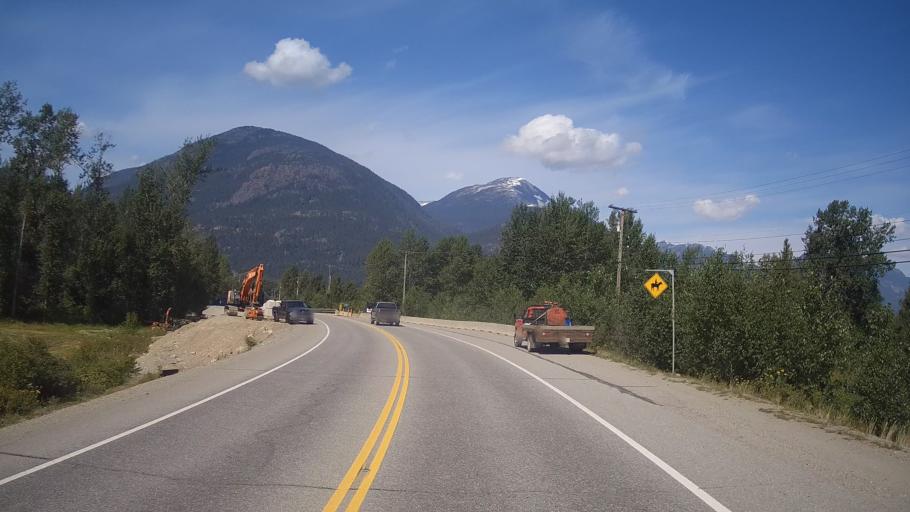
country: CA
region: British Columbia
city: Pemberton
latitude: 50.3162
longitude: -122.7658
